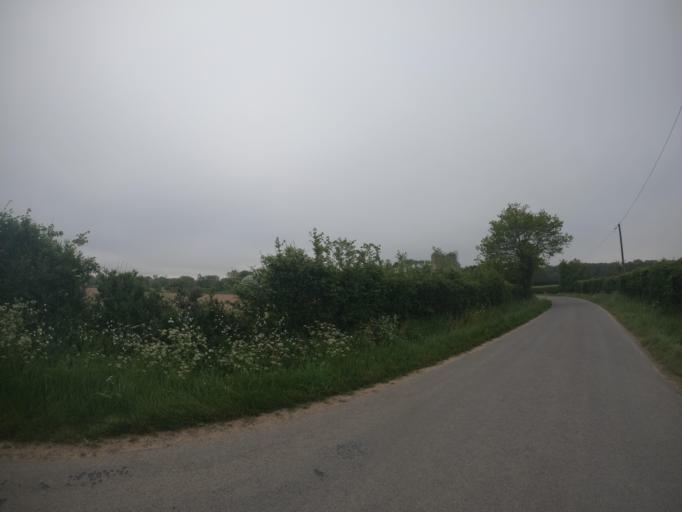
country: FR
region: Poitou-Charentes
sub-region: Departement des Deux-Sevres
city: Chiche
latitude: 46.8595
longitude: -0.3444
